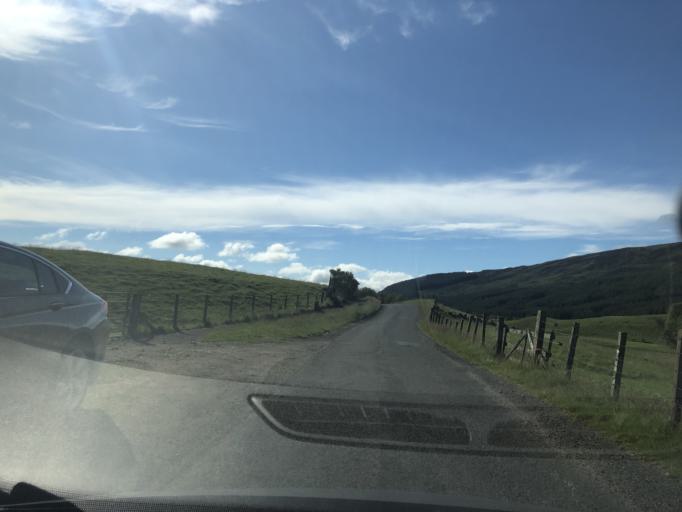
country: GB
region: Scotland
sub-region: Angus
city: Kirriemuir
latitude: 56.8416
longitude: -3.0944
